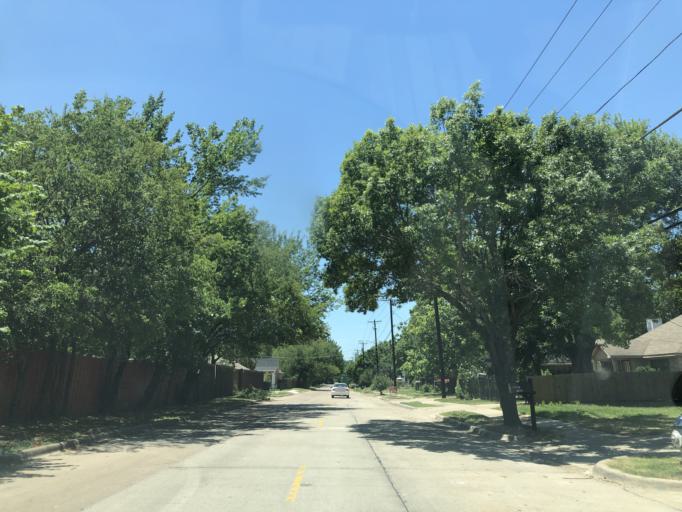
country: US
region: Texas
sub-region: Dallas County
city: Cockrell Hill
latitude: 32.7928
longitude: -96.8877
